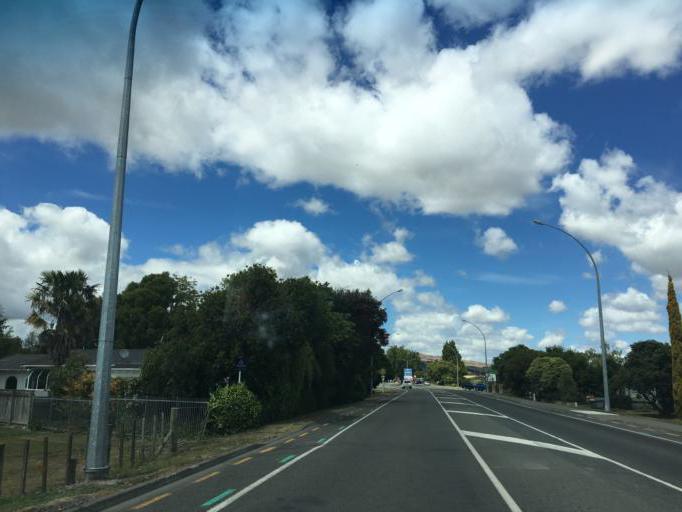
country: NZ
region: Hawke's Bay
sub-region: Hastings District
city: Hastings
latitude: -39.6602
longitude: 176.8849
